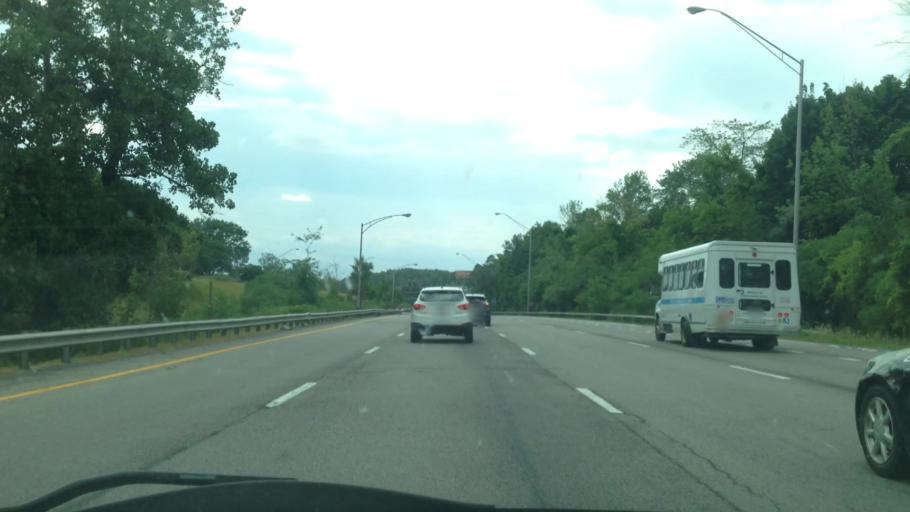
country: US
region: New York
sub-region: Monroe County
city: North Gates
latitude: 43.1523
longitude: -77.6800
